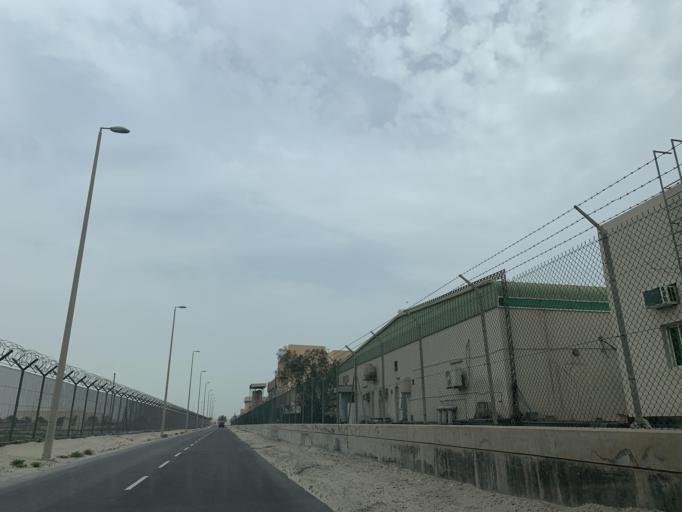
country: BH
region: Muharraq
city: Al Hadd
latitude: 26.2214
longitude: 50.6664
